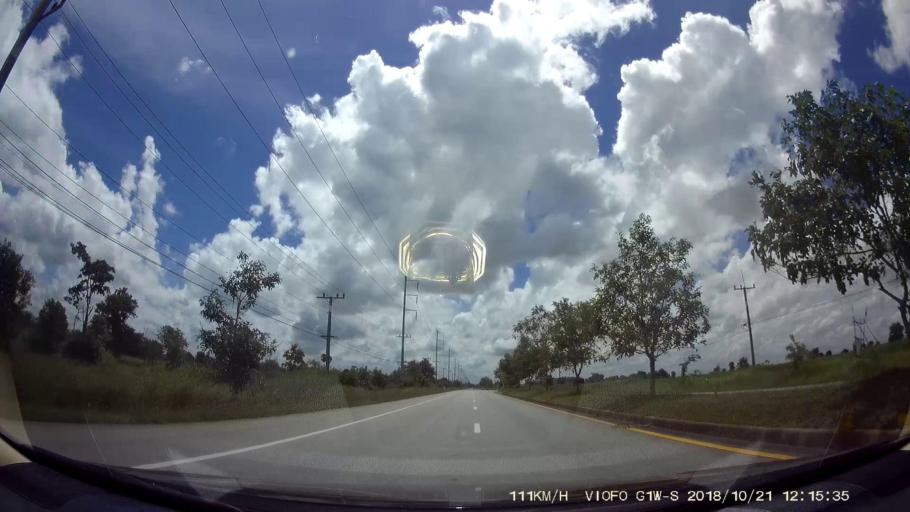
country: TH
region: Nakhon Ratchasima
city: Dan Khun Thot
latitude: 15.3606
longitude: 101.8299
